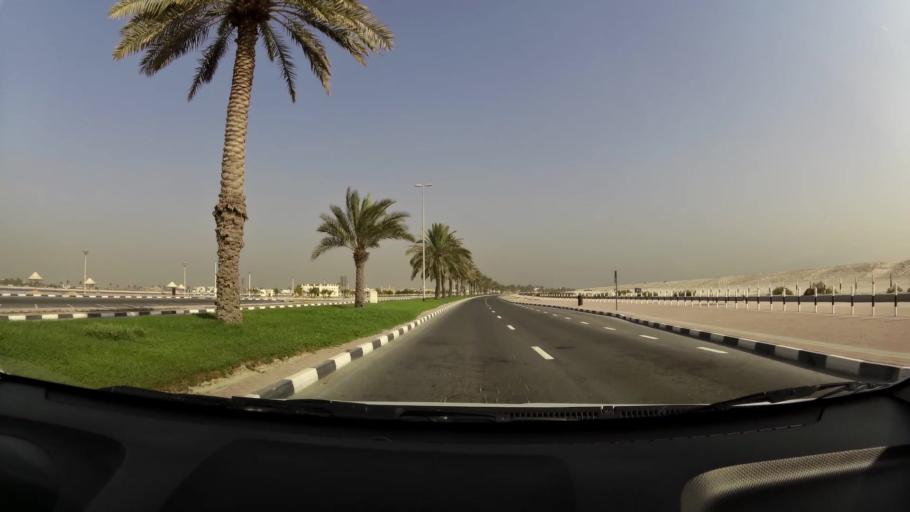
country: AE
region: Ash Shariqah
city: Sharjah
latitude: 25.3051
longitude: 55.3563
